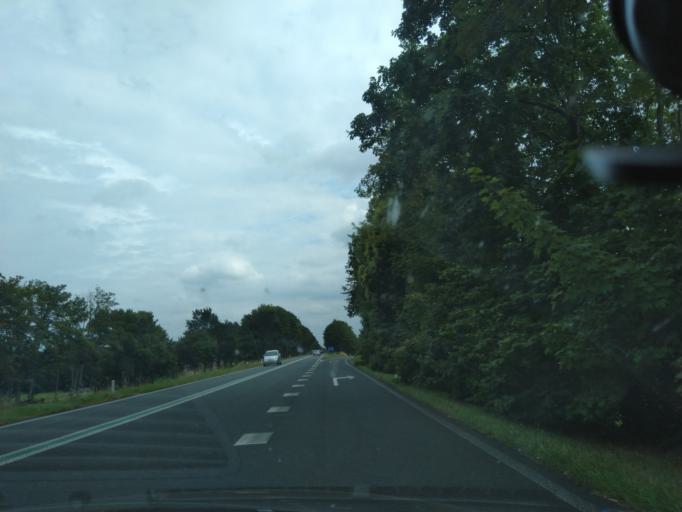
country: NL
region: Groningen
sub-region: Gemeente  Oldambt
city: Winschoten
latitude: 53.1029
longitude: 7.0707
